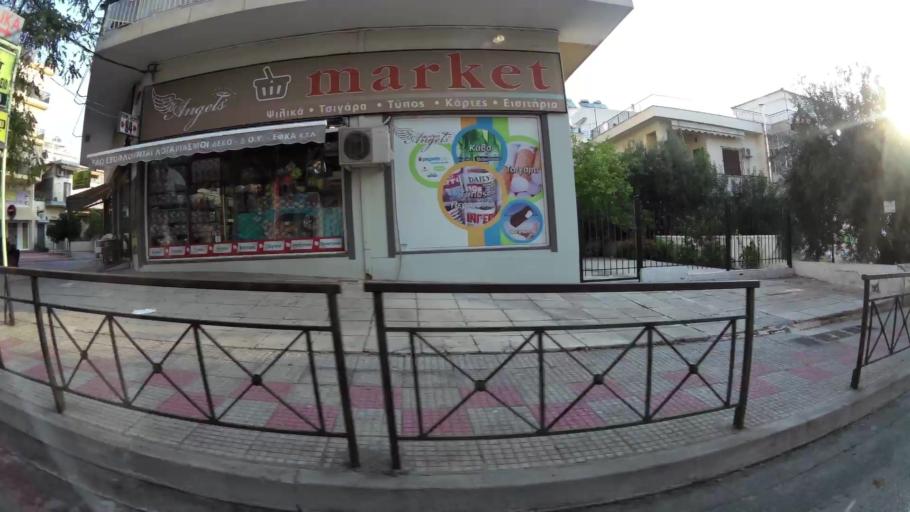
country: GR
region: Attica
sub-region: Nomarchia Athinas
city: Petroupolis
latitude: 38.0350
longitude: 23.6779
